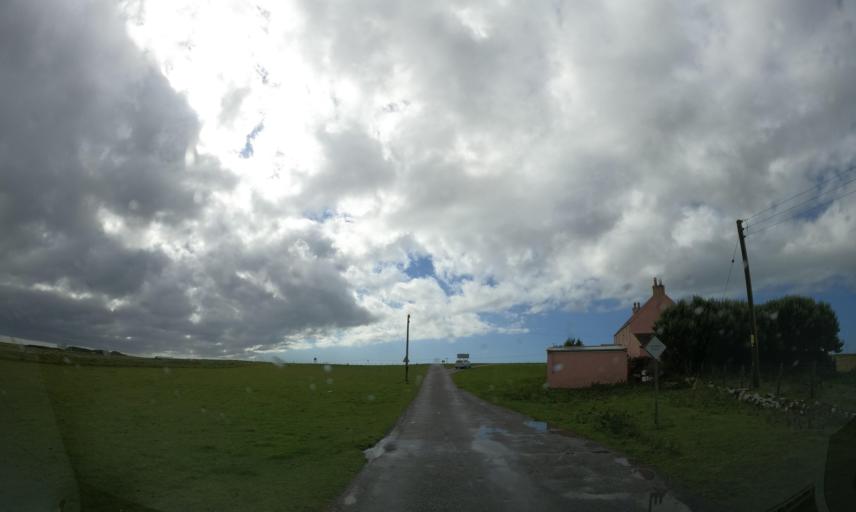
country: GB
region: Scotland
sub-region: Eilean Siar
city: Barra
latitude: 56.5139
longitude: -6.8163
